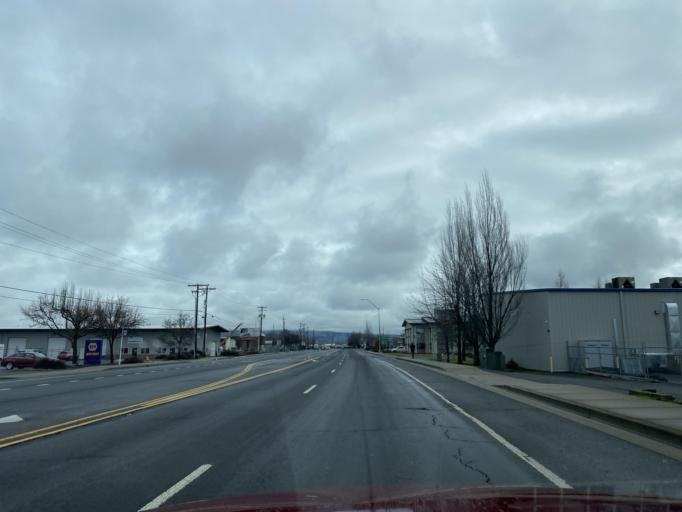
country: US
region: Oregon
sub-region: Jackson County
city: Medford
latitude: 42.3407
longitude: -122.8979
